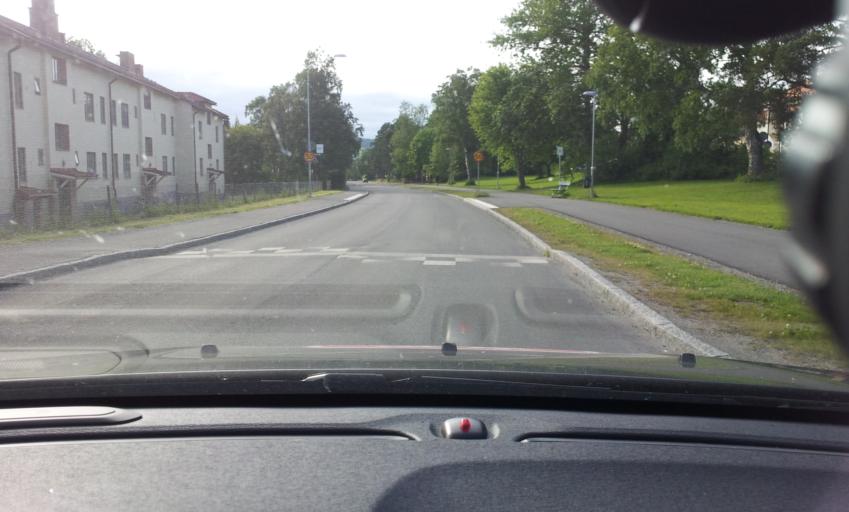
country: SE
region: Jaemtland
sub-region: OEstersunds Kommun
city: Ostersund
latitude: 63.1661
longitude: 14.6573
